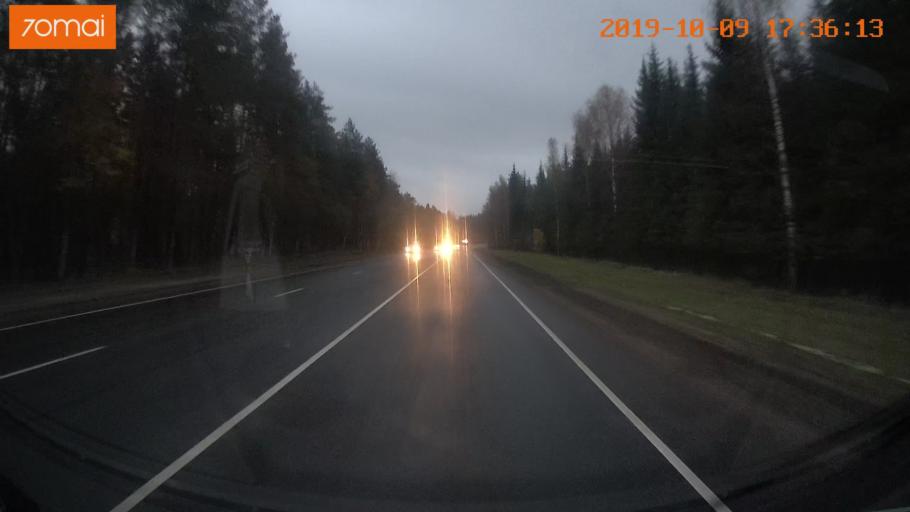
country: RU
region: Ivanovo
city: Bogorodskoye
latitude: 57.0817
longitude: 40.9981
